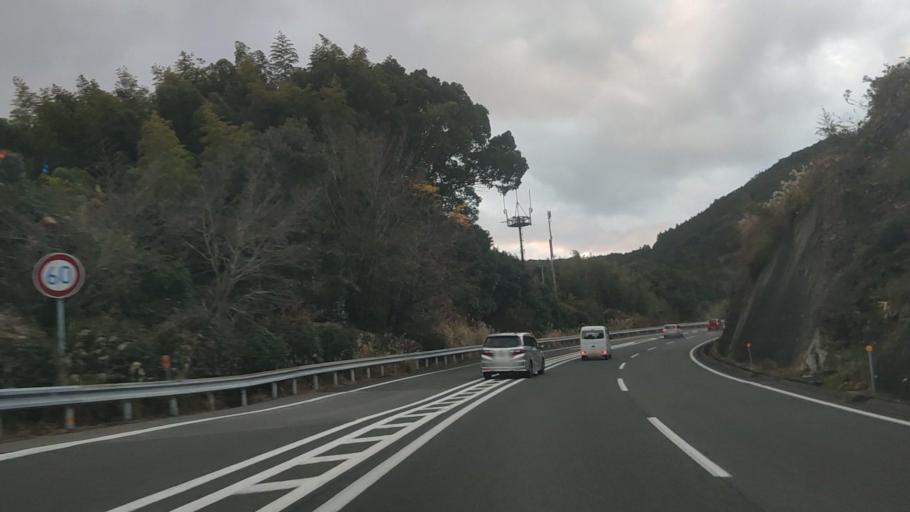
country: JP
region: Nagasaki
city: Obita
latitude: 32.8111
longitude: 129.9353
